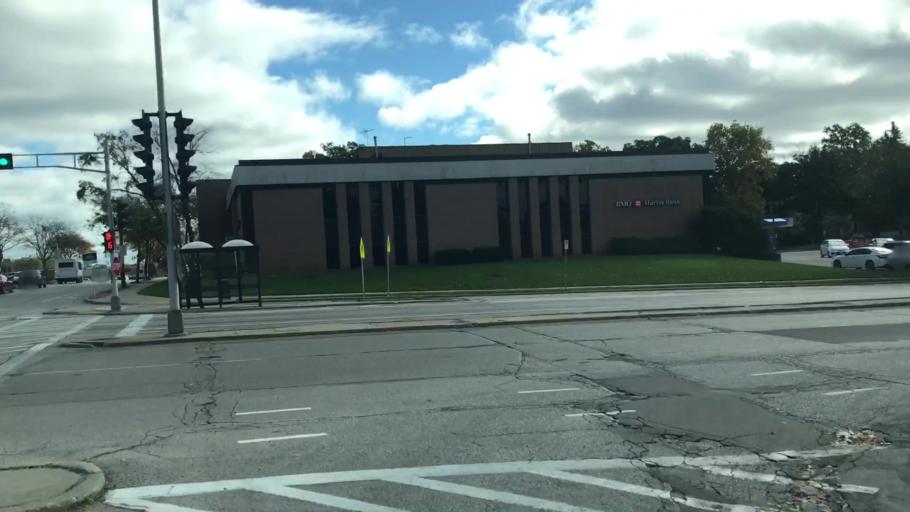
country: US
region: Wisconsin
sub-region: Milwaukee County
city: Wauwatosa
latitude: 43.0606
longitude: -88.0077
